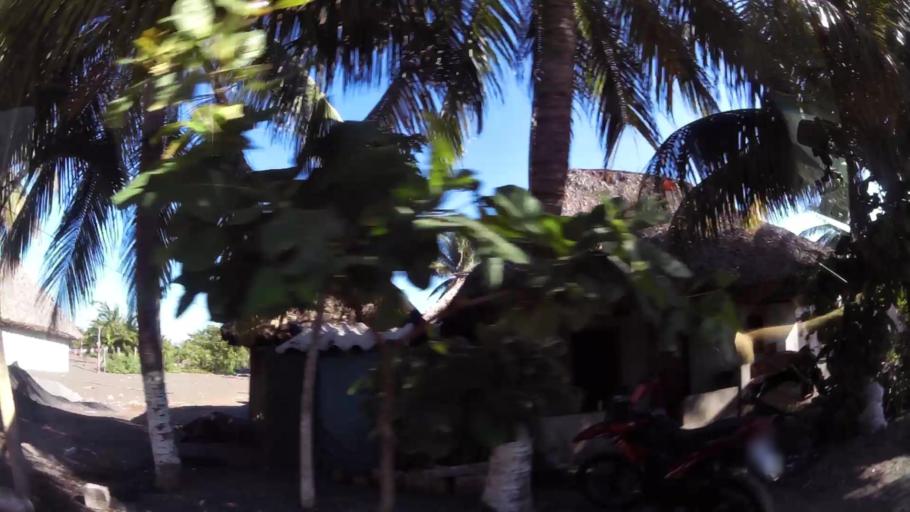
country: GT
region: Santa Rosa
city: Guazacapan
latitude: 13.8616
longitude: -90.4013
